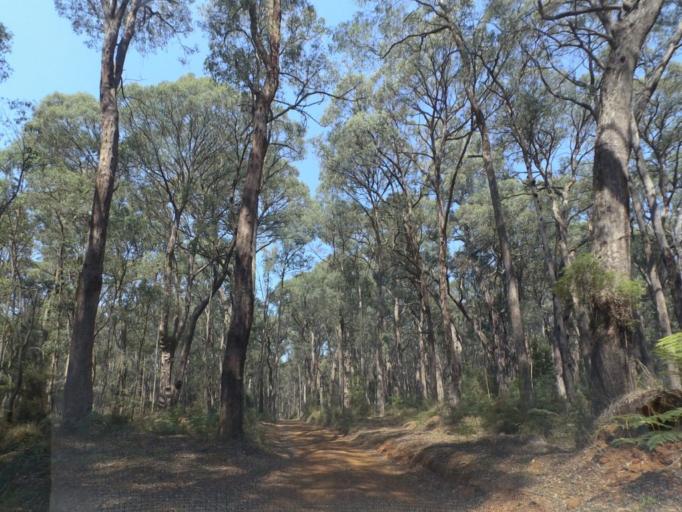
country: AU
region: Victoria
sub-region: Yarra Ranges
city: Healesville
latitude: -37.5745
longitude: 145.6602
